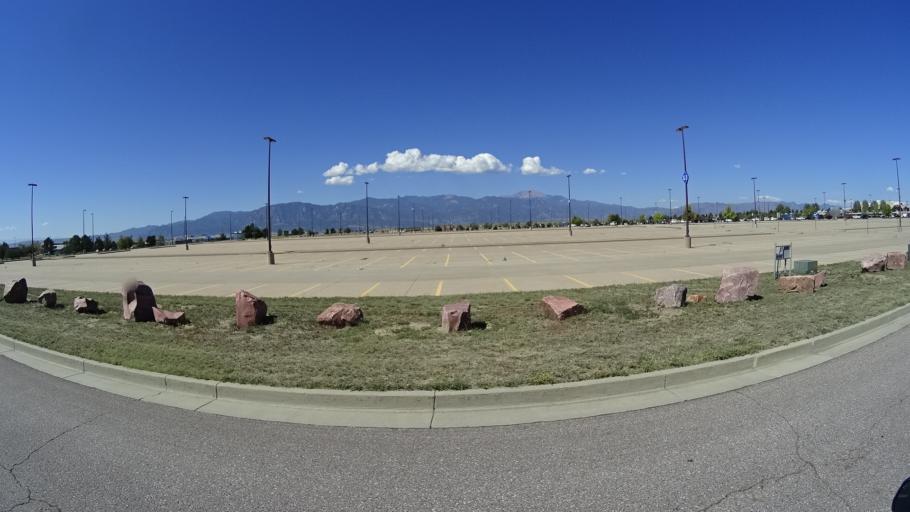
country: US
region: Colorado
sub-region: El Paso County
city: Security-Widefield
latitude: 38.7929
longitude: -104.6977
